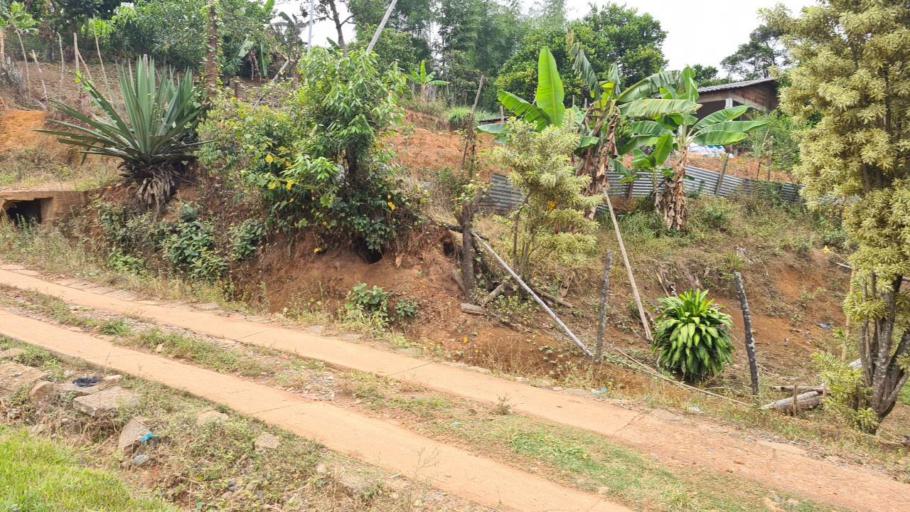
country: CO
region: Cauca
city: Buenos Aires
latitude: 3.1202
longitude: -76.6047
